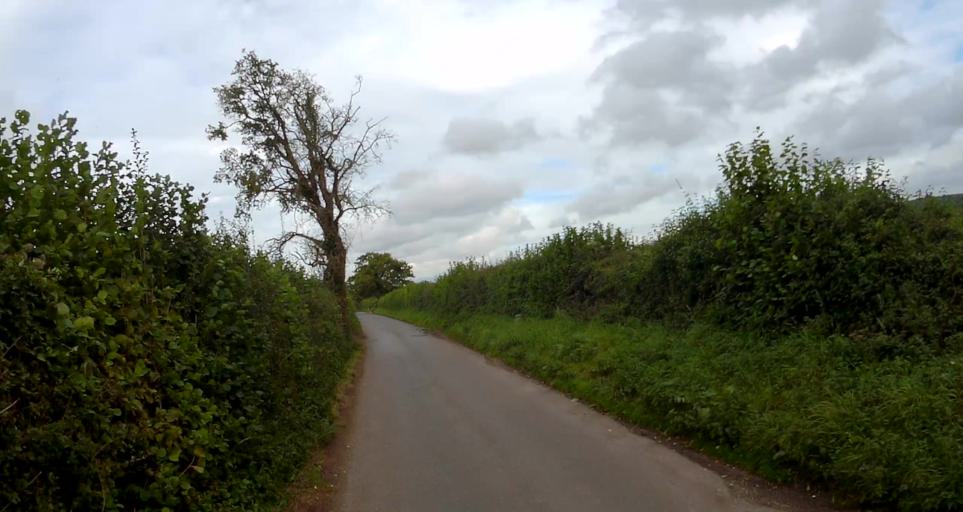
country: GB
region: England
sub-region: Hampshire
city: Four Marks
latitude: 51.1036
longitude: -1.1374
